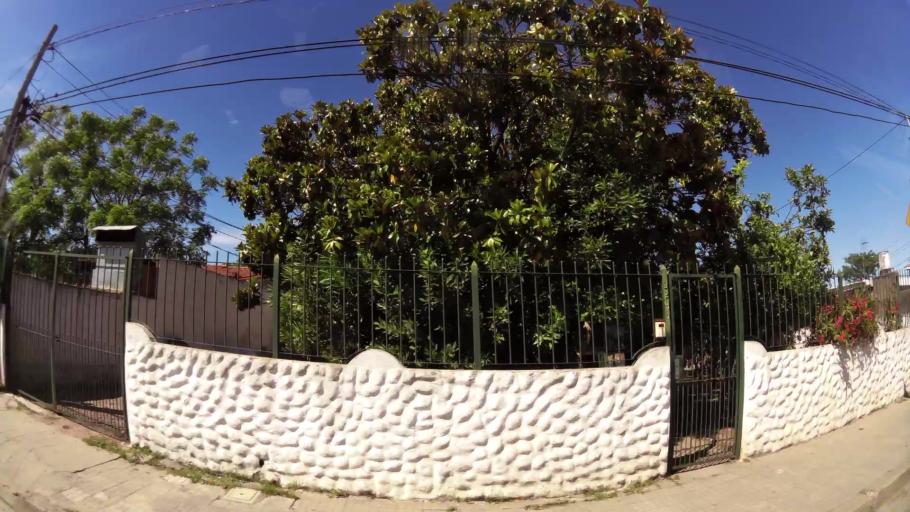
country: UY
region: Canelones
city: Paso de Carrasco
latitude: -34.8486
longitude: -56.1234
